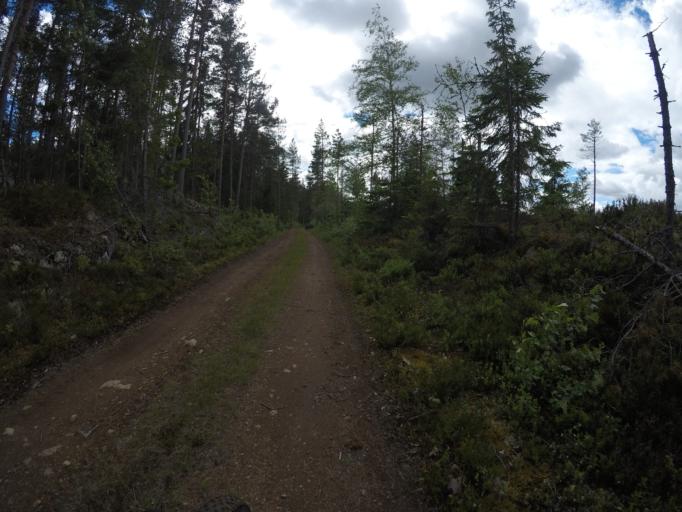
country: SE
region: Vaermland
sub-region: Filipstads Kommun
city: Lesjofors
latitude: 60.1410
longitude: 14.2686
